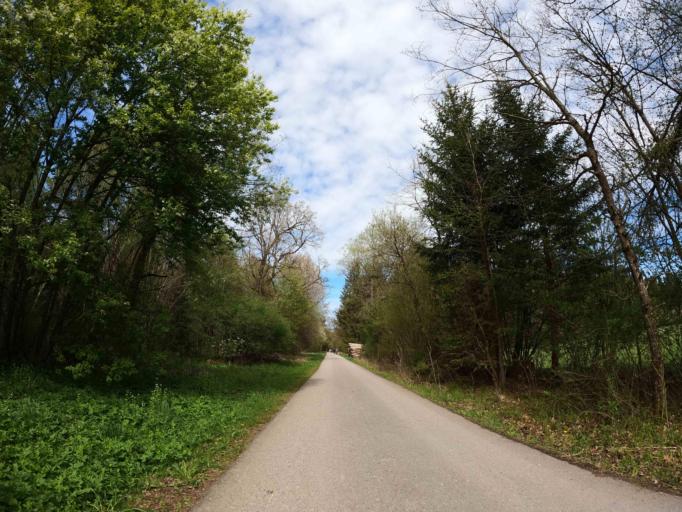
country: DE
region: Bavaria
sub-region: Upper Bavaria
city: Grunwald
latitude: 48.0315
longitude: 11.5487
